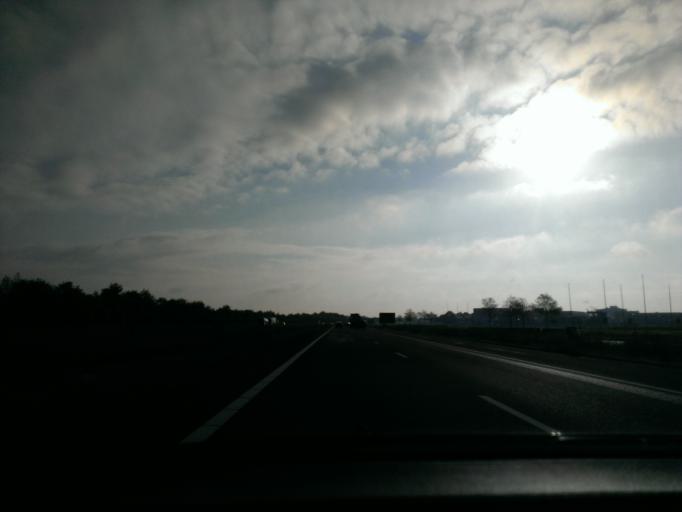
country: NL
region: Drenthe
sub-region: Gemeente Hoogeveen
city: Hoogeveen
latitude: 52.7126
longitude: 6.5017
